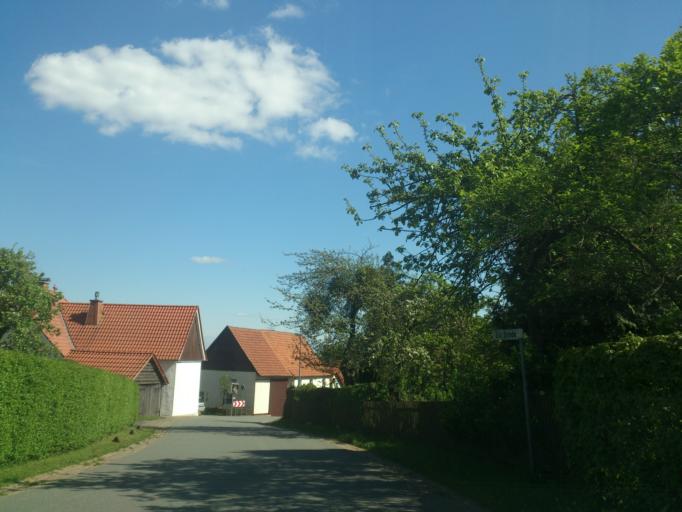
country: DE
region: North Rhine-Westphalia
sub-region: Regierungsbezirk Detmold
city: Willebadessen
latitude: 51.6506
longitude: 9.0465
